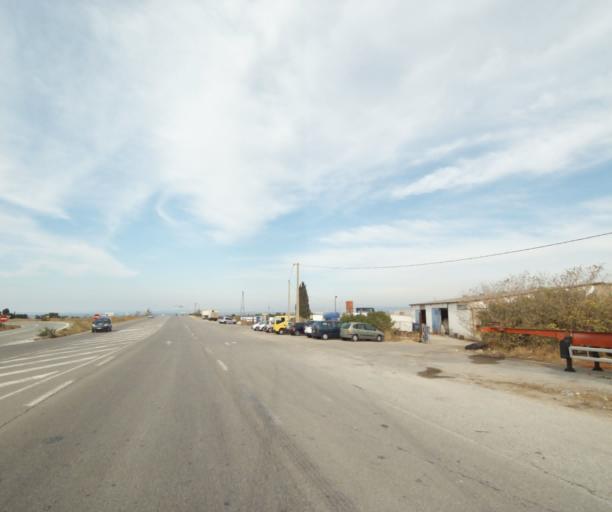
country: FR
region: Provence-Alpes-Cote d'Azur
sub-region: Departement des Bouches-du-Rhone
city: Gignac-la-Nerthe
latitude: 43.3779
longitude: 5.2255
